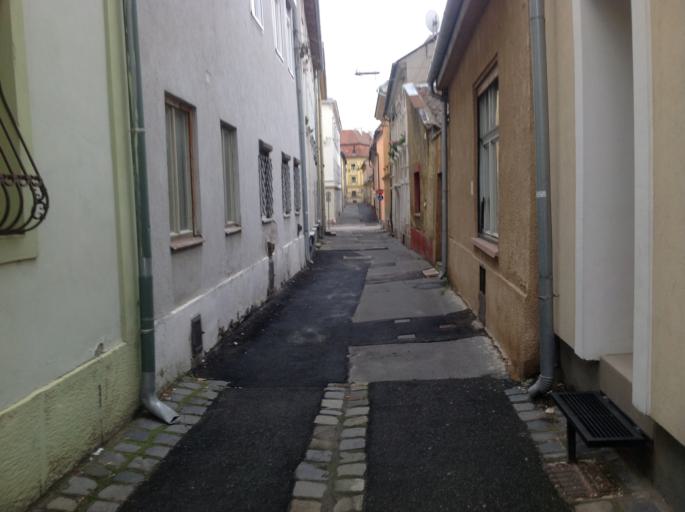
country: HU
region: Gyor-Moson-Sopron
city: Gyor
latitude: 47.6898
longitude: 17.6369
